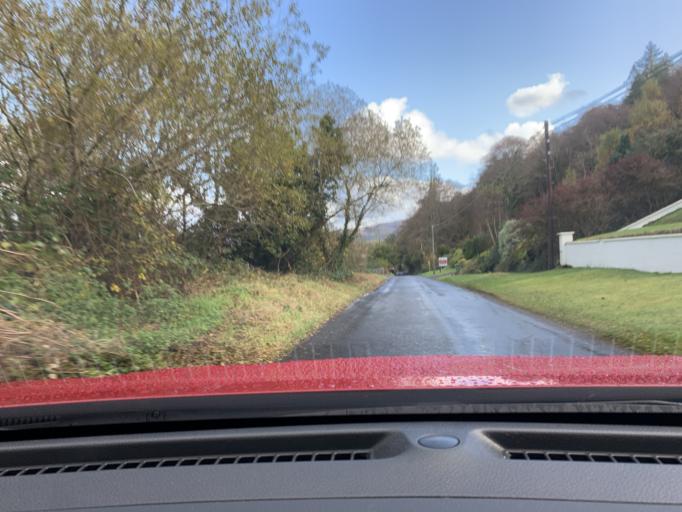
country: IE
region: Connaught
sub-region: Sligo
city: Sligo
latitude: 54.2574
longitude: -8.4494
